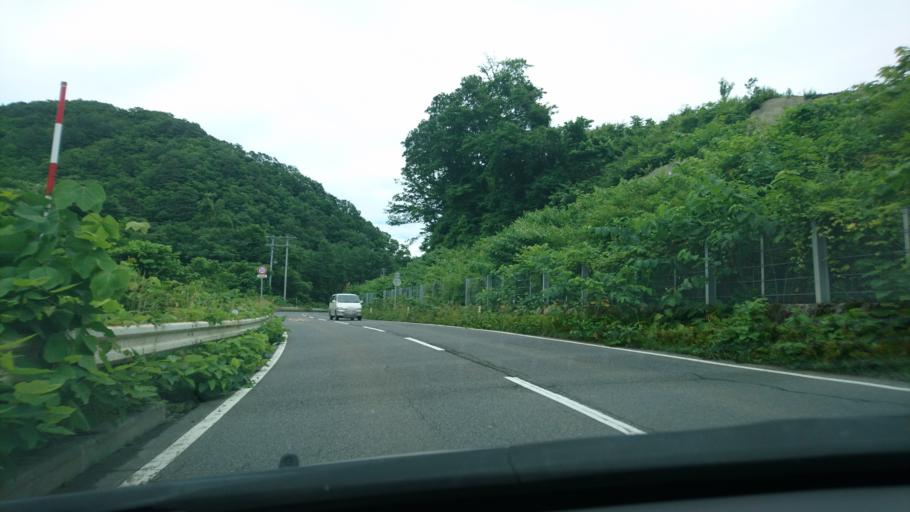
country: JP
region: Iwate
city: Miyako
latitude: 39.9906
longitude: 141.8756
